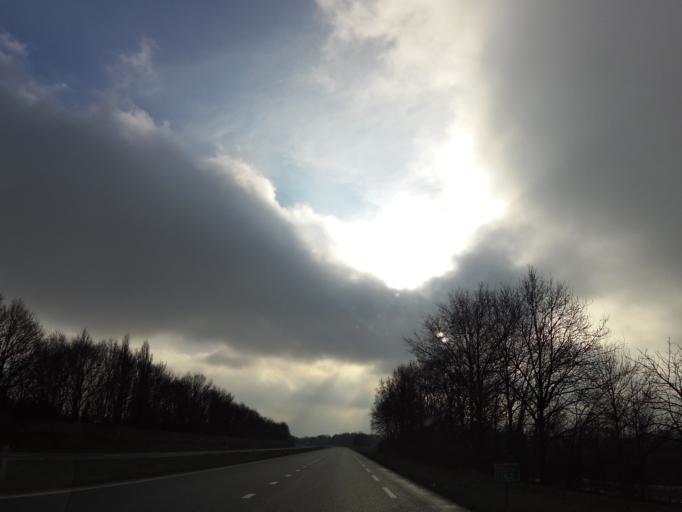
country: NL
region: Limburg
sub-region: Gemeente Gennep
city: Gennep
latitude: 51.7005
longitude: 5.9641
